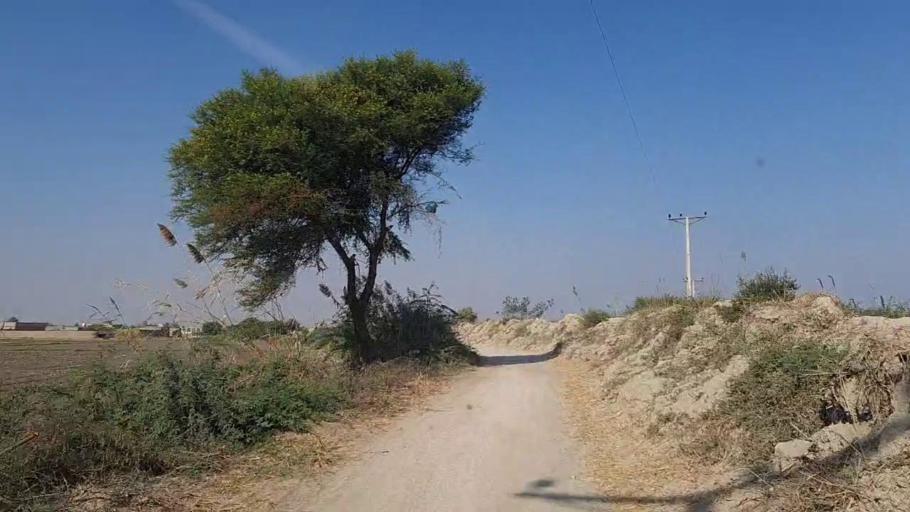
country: PK
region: Sindh
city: Thatta
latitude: 24.7685
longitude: 67.9324
